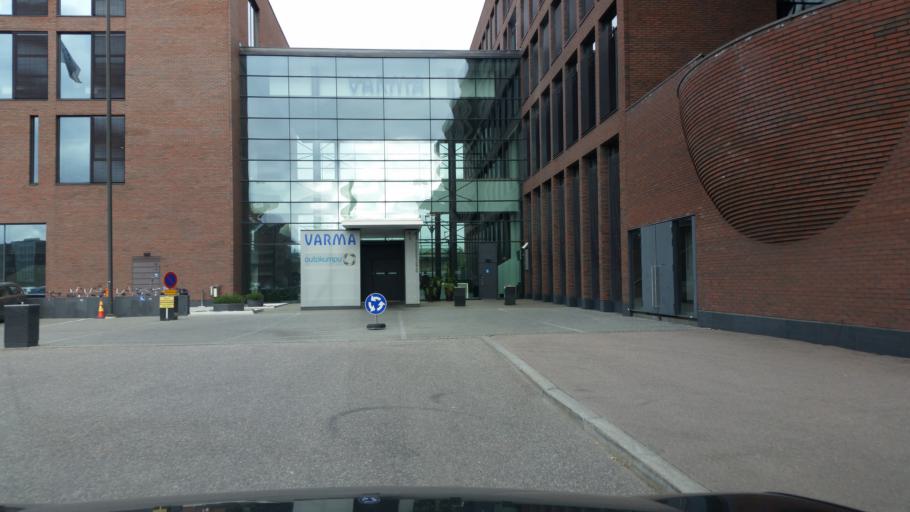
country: FI
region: Uusimaa
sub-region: Helsinki
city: Helsinki
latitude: 60.1659
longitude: 24.8995
